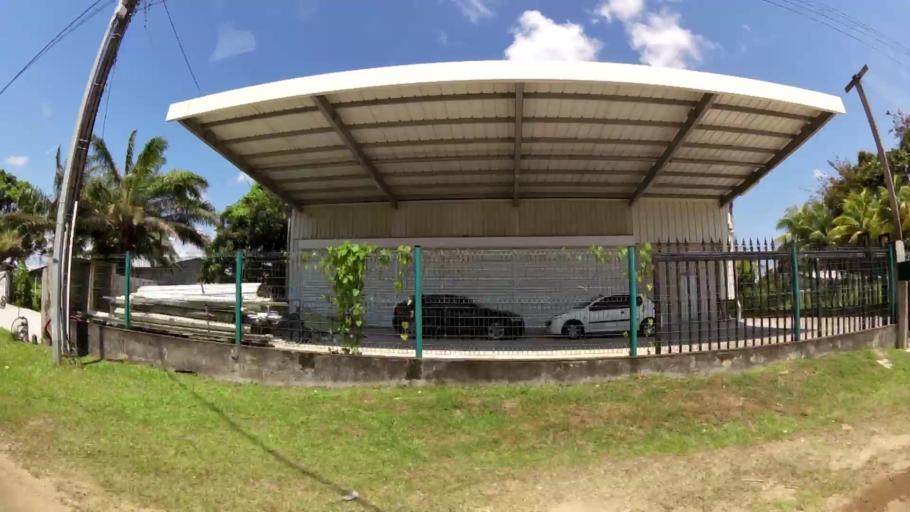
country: GF
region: Guyane
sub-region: Guyane
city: Cayenne
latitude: 4.9026
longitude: -52.3258
